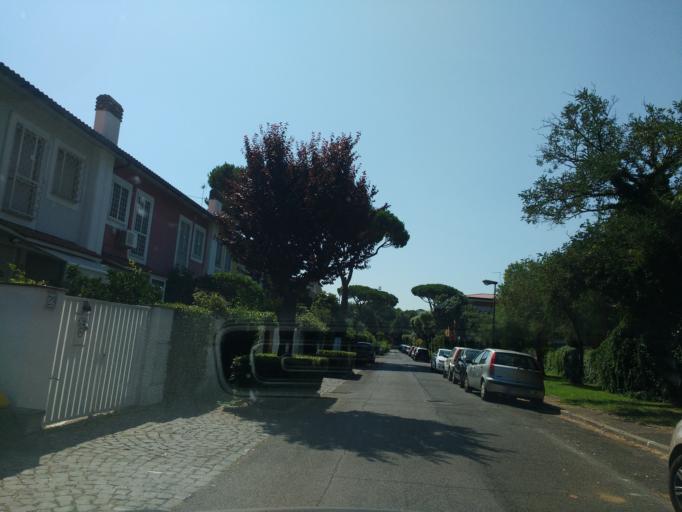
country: IT
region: Latium
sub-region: Citta metropolitana di Roma Capitale
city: Acilia-Castel Fusano-Ostia Antica
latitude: 41.7566
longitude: 12.3571
